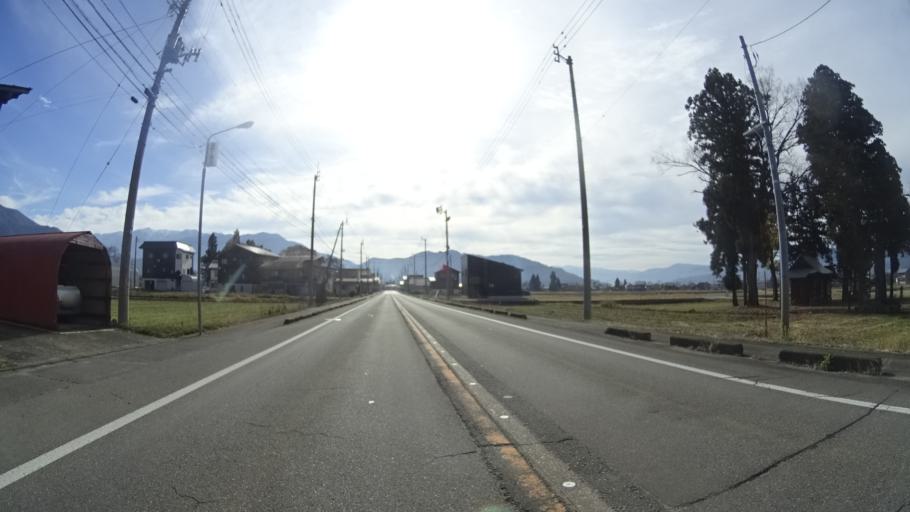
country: JP
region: Niigata
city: Muikamachi
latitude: 37.1012
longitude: 138.9198
